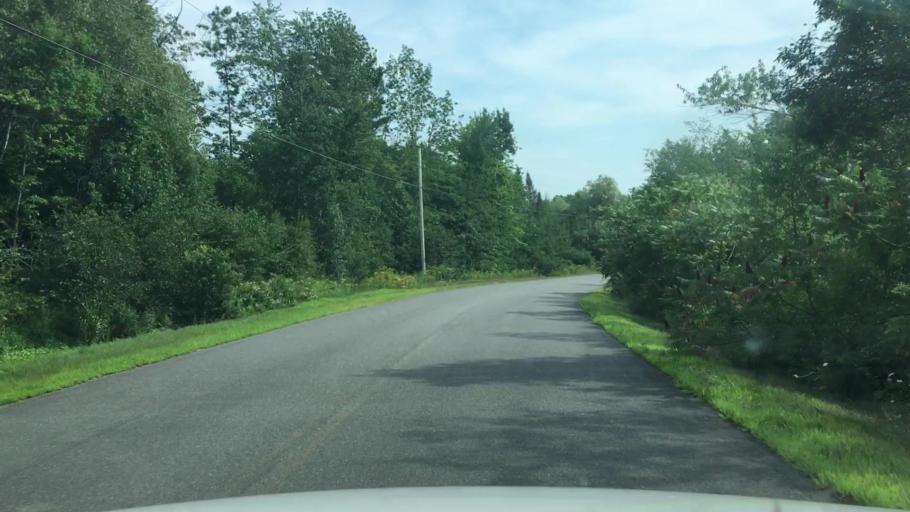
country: US
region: Maine
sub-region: Lincoln County
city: Jefferson
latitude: 44.2383
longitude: -69.4437
